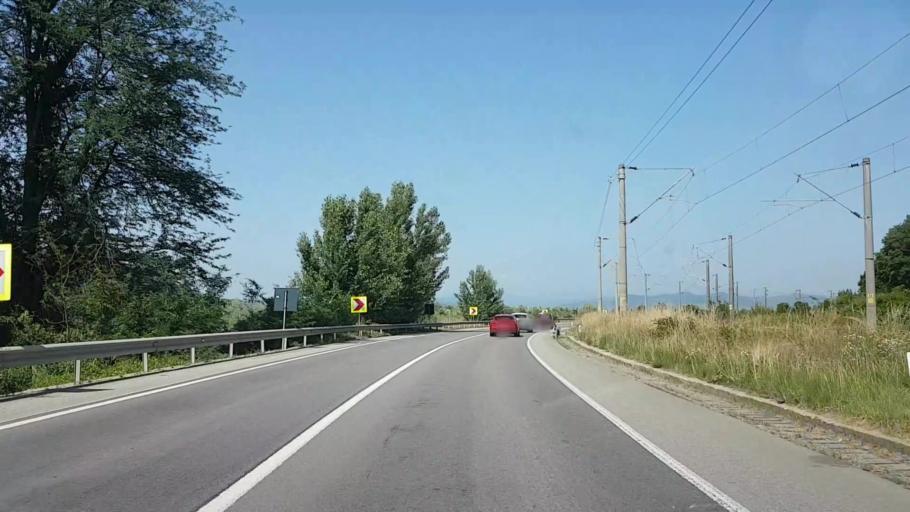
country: RO
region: Bistrita-Nasaud
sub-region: Comuna Beclean
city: Beclean
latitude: 47.1851
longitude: 24.1934
